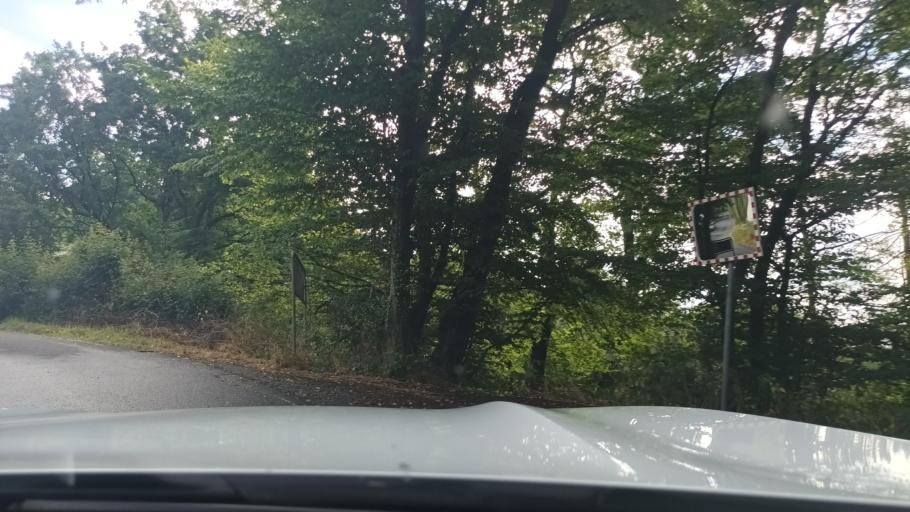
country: DE
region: North Rhine-Westphalia
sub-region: Regierungsbezirk Koln
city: Hennef
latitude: 50.7351
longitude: 7.3183
